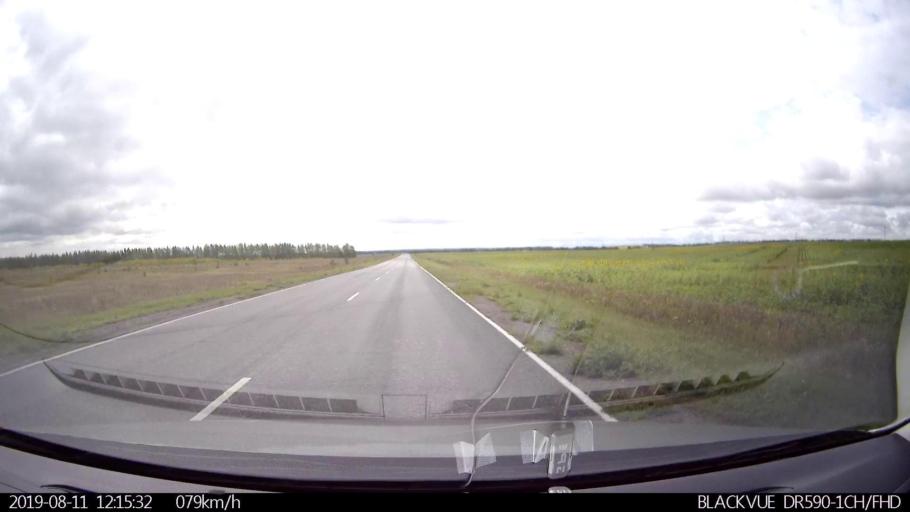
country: RU
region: Ulyanovsk
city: Ignatovka
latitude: 53.9407
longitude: 47.9676
